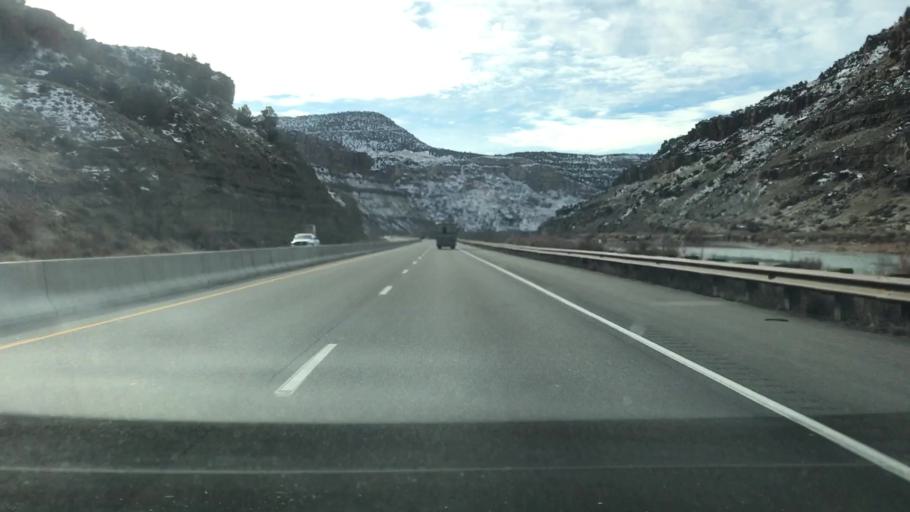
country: US
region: Colorado
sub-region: Mesa County
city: Palisade
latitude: 39.2202
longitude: -108.2562
